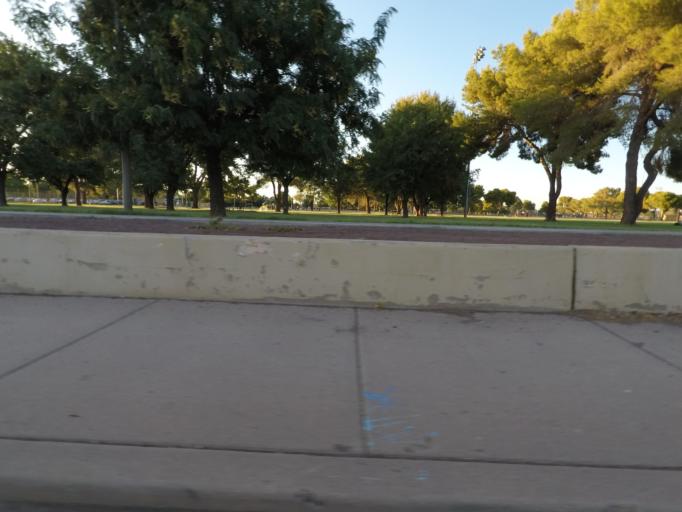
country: US
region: Arizona
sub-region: Maricopa County
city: Glendale
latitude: 33.5022
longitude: -112.1314
